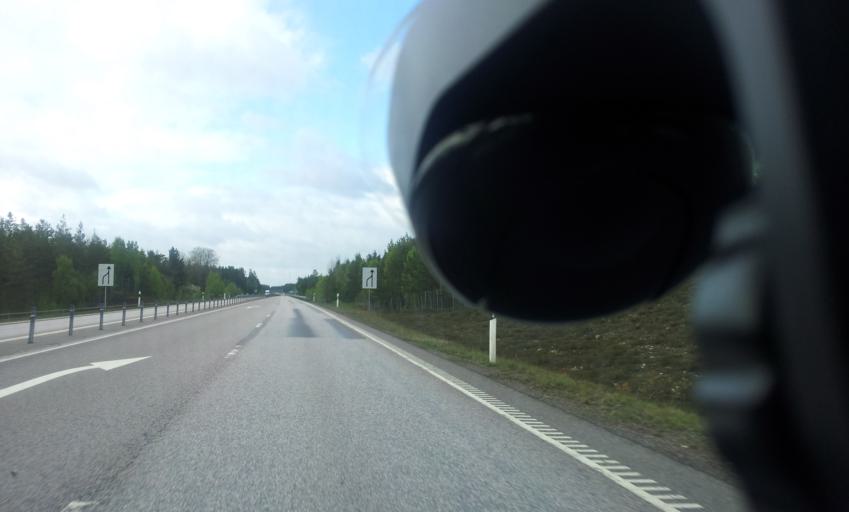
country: SE
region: Kalmar
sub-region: Torsas Kommun
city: Torsas
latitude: 56.4816
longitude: 16.0818
